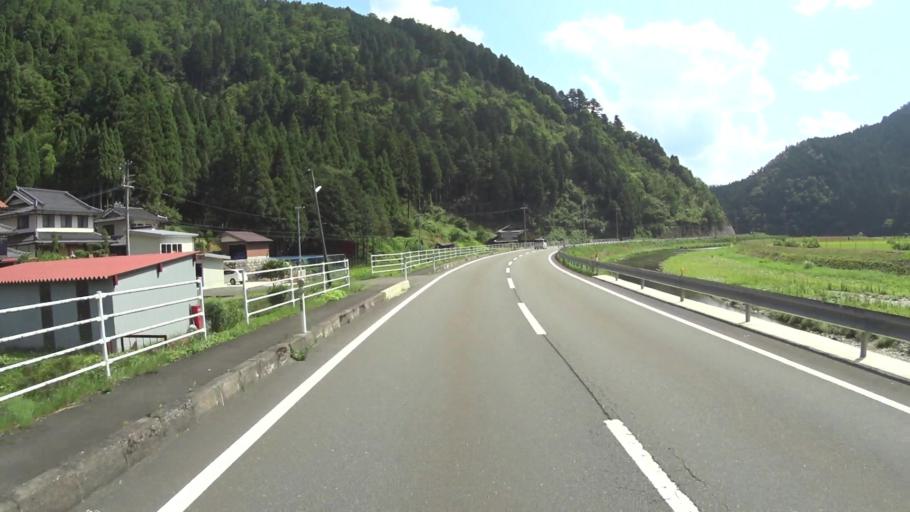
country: JP
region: Fukui
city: Obama
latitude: 35.3295
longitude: 135.5669
